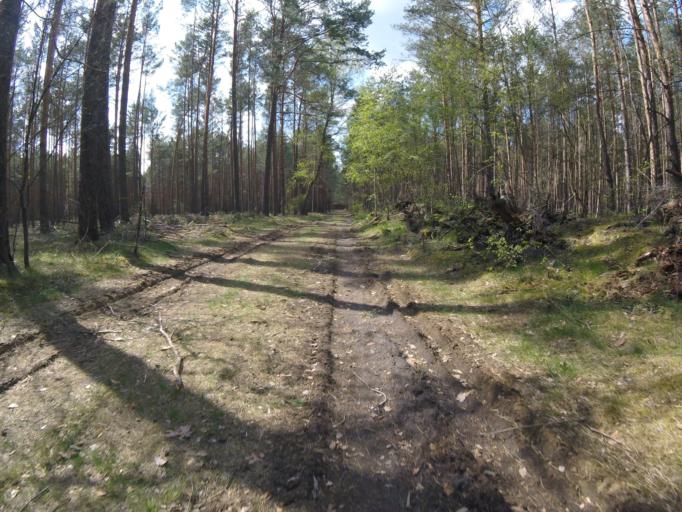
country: DE
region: Brandenburg
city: Gross Koris
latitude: 52.1987
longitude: 13.6989
